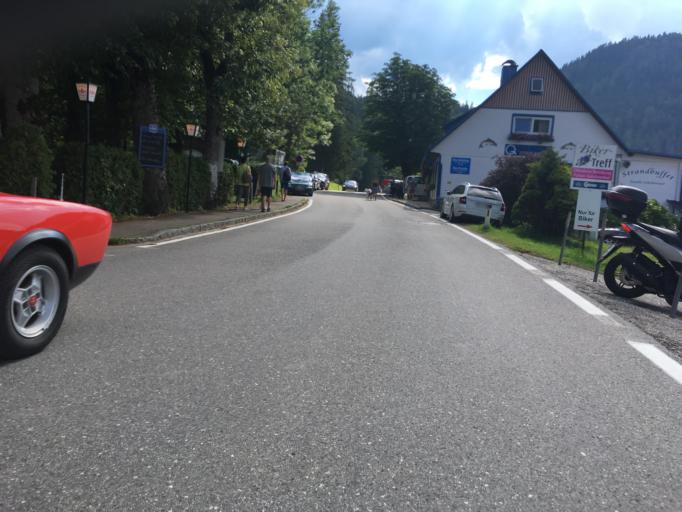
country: AT
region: Lower Austria
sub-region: Politischer Bezirk Lilienfeld
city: Mitterbach am Erlaufsee
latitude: 47.7904
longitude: 15.2810
